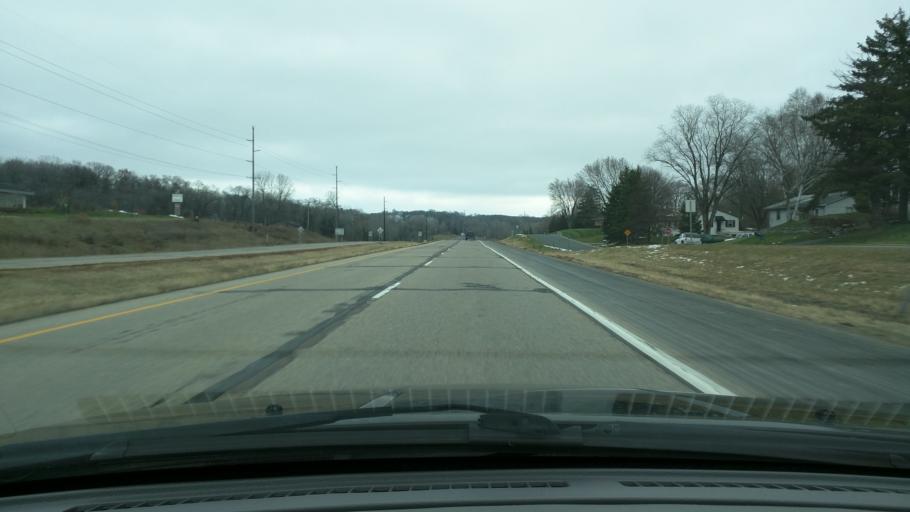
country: US
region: Minnesota
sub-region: Dakota County
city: Mendota Heights
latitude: 44.8452
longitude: -93.1199
